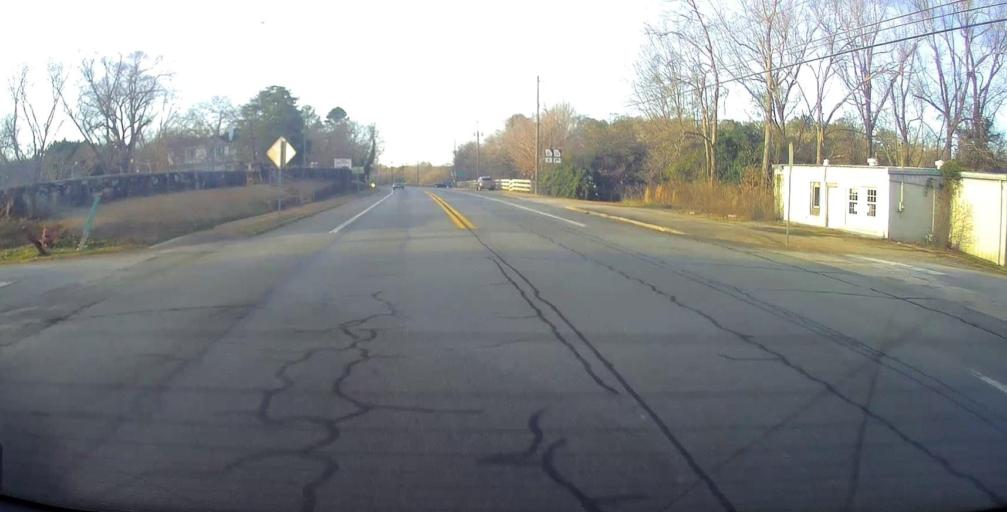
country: US
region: Georgia
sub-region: Talbot County
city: Sardis
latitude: 32.7861
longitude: -84.5612
